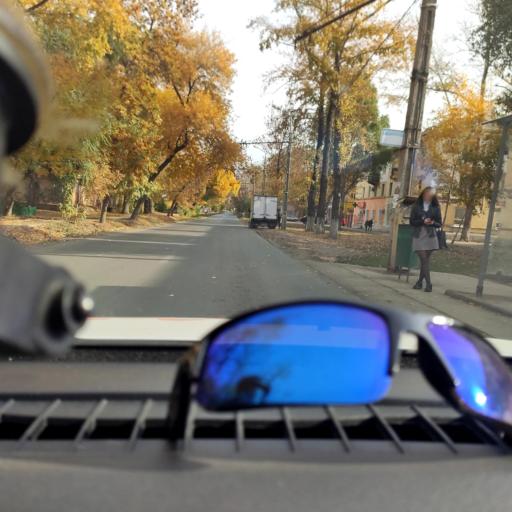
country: RU
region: Samara
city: Samara
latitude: 53.1145
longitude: 50.0755
